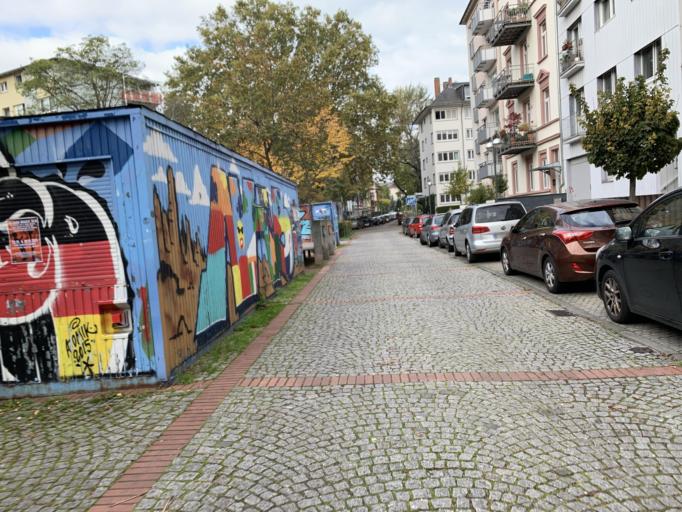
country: DE
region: Hesse
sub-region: Regierungsbezirk Darmstadt
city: Frankfurt am Main
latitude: 50.1207
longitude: 8.6952
